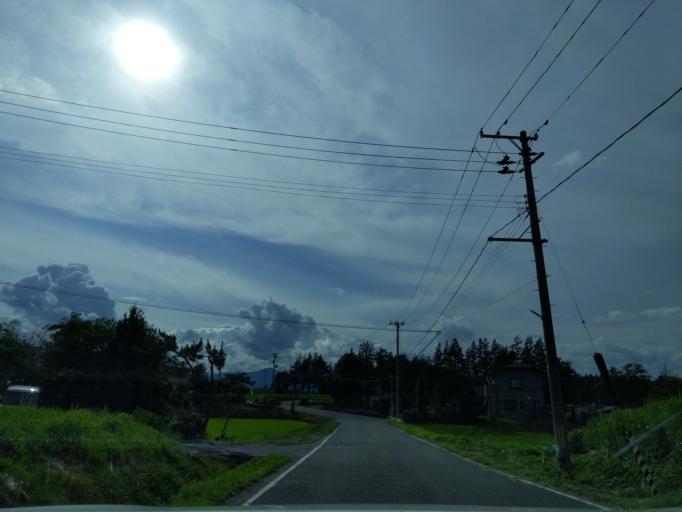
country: JP
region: Fukushima
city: Koriyama
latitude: 37.3452
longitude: 140.3220
